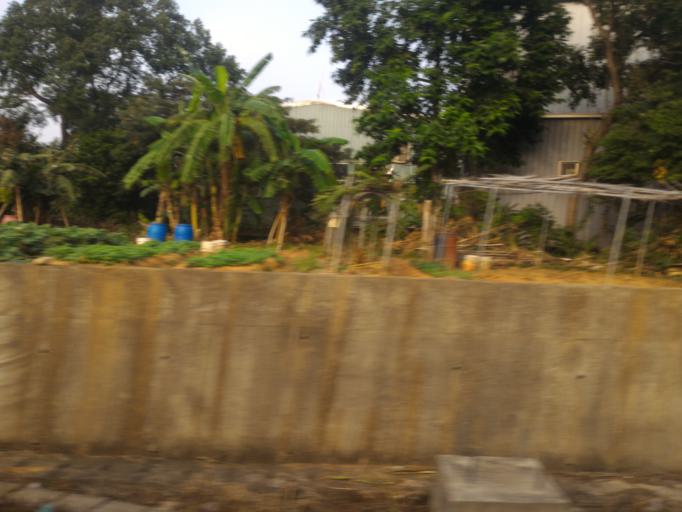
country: TW
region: Taiwan
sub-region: Taoyuan
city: Taoyuan
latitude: 24.9490
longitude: 121.3381
